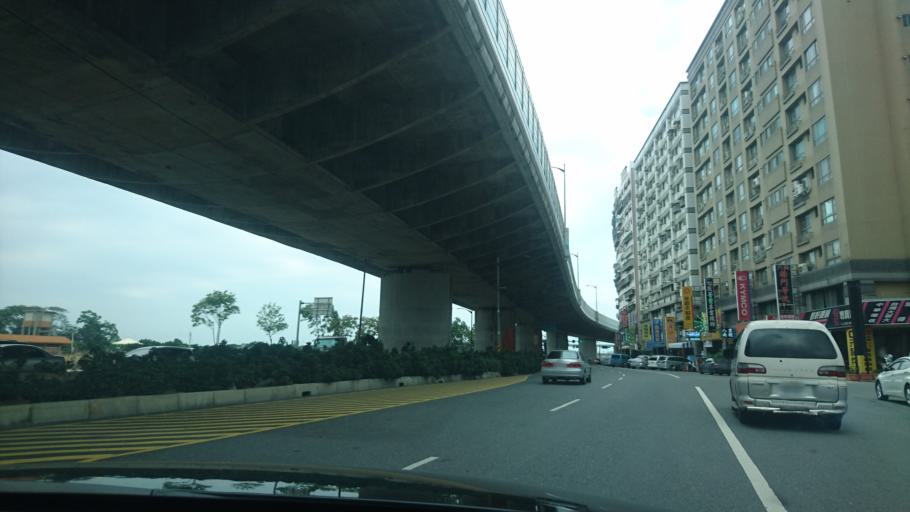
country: TW
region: Taipei
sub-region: Taipei
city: Banqiao
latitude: 25.1441
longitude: 121.3976
